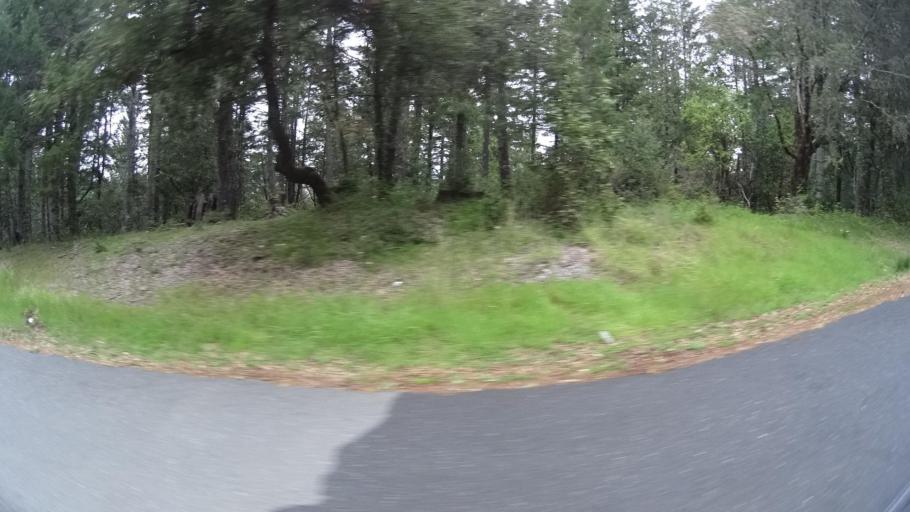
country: US
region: California
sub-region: Humboldt County
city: Redway
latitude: 40.2734
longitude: -123.7787
